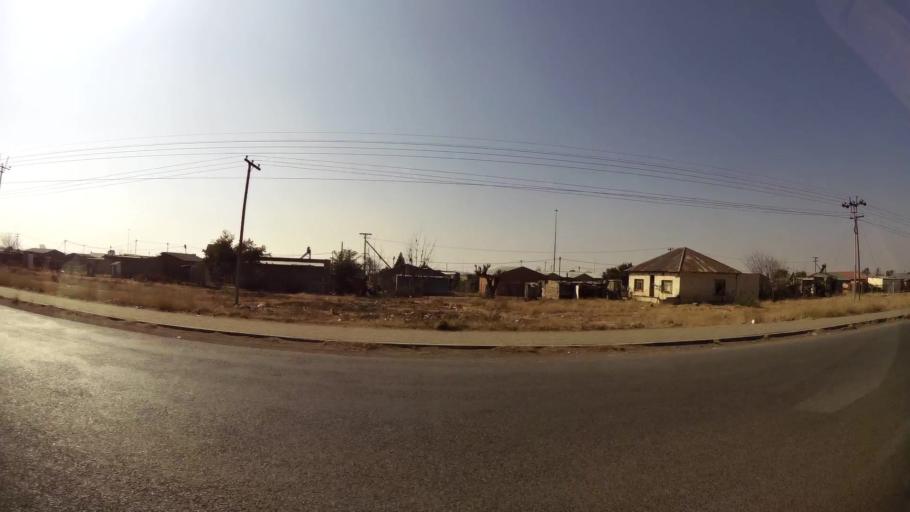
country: ZA
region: Orange Free State
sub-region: Mangaung Metropolitan Municipality
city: Bloemfontein
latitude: -29.1699
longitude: 26.2612
